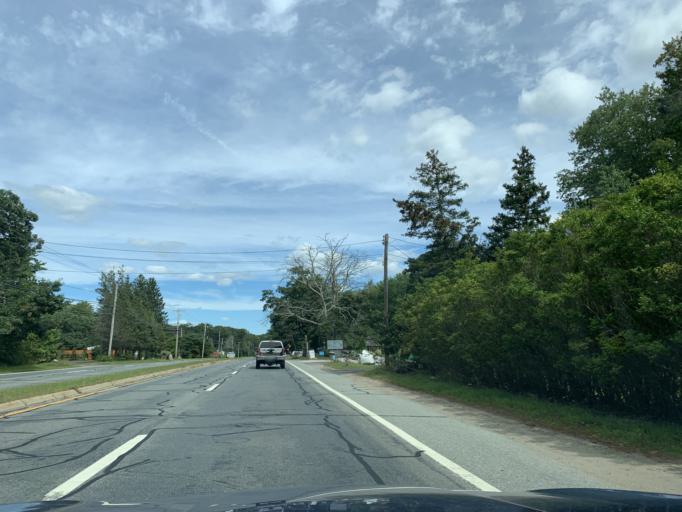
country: US
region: Rhode Island
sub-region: Kent County
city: West Greenwich
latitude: 41.5874
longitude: -71.6513
